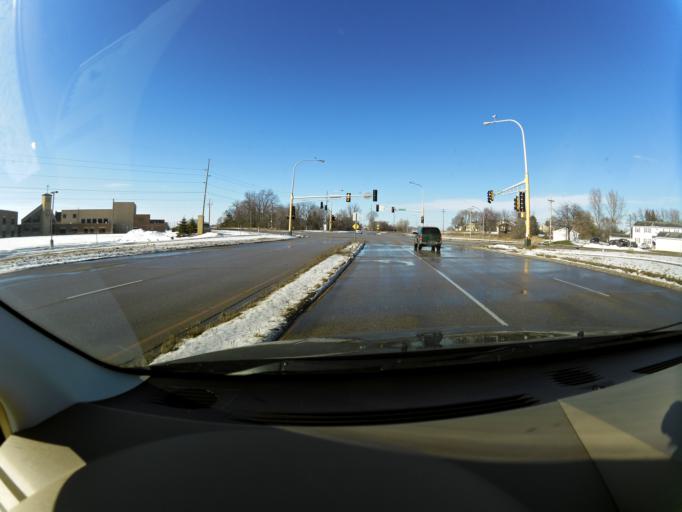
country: US
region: Minnesota
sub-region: Olmsted County
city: Rochester
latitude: 44.0432
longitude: -92.5016
